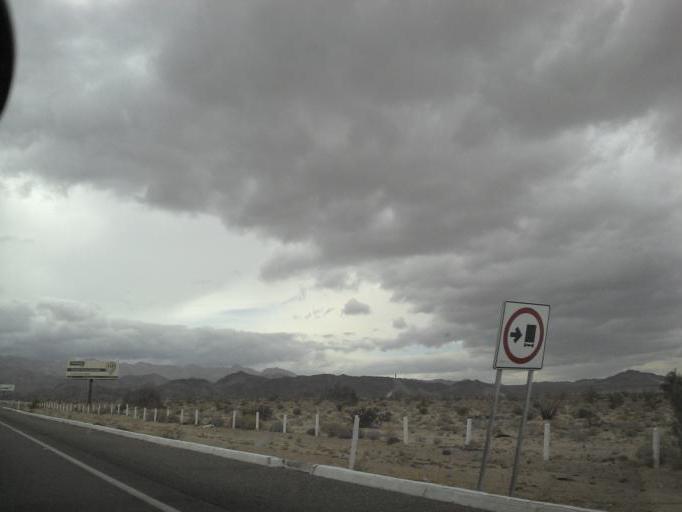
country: US
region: California
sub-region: Imperial County
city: Seeley
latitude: 32.5660
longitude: -115.9086
